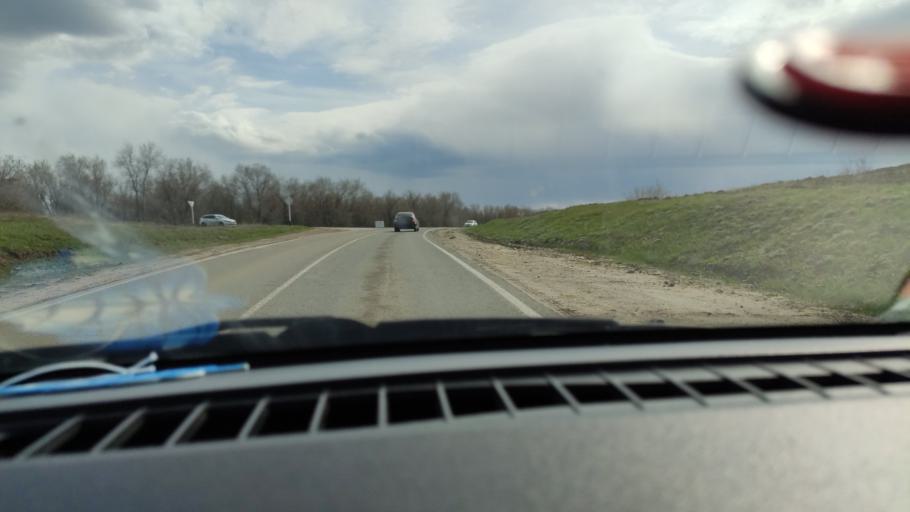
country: RU
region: Saratov
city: Privolzhskiy
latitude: 51.3440
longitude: 46.0425
